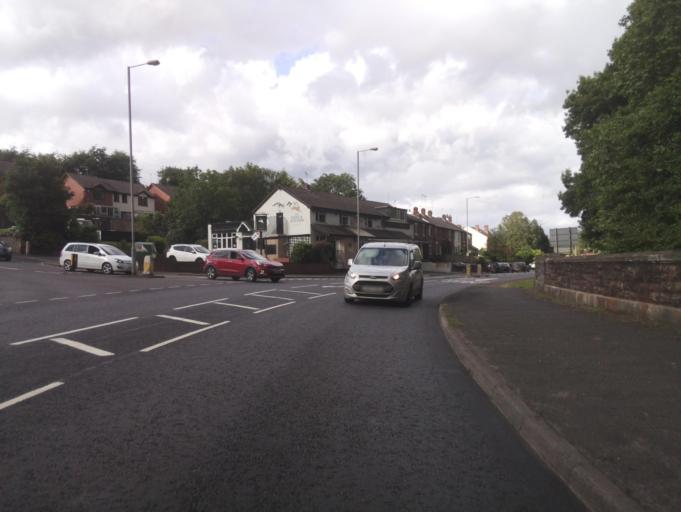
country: GB
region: England
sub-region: Worcestershire
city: Kidderminster
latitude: 52.3995
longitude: -2.2365
